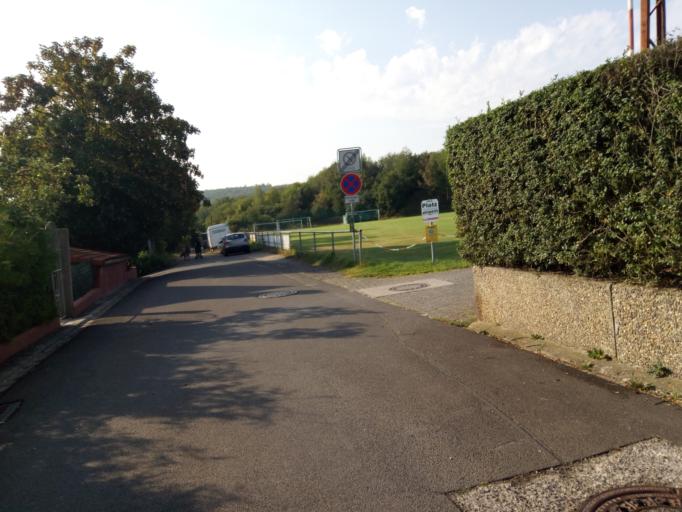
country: DE
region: Rheinland-Pfalz
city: Waldlaubersheim
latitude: 49.9262
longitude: 7.8300
